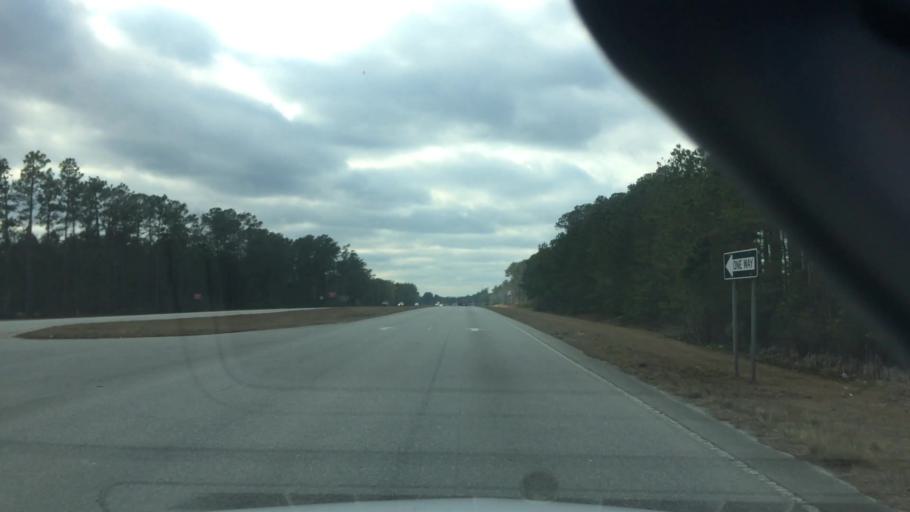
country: US
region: North Carolina
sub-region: Brunswick County
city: Bolivia
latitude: 34.0437
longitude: -78.2362
